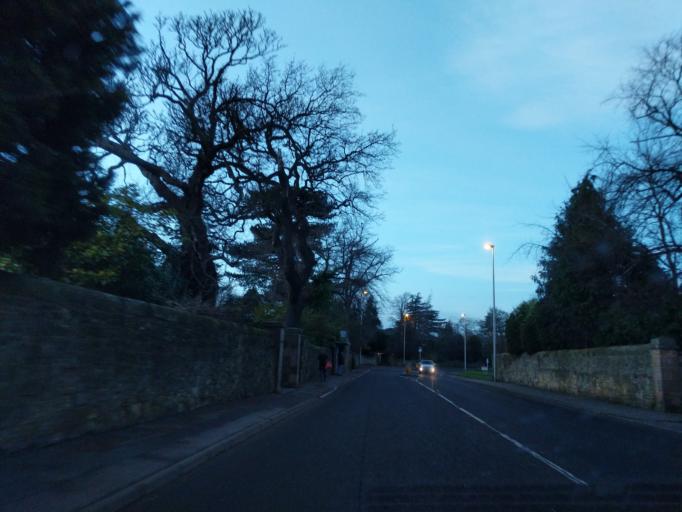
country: GB
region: Scotland
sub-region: Midlothian
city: Bonnyrigg
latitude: 55.8800
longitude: -3.1096
